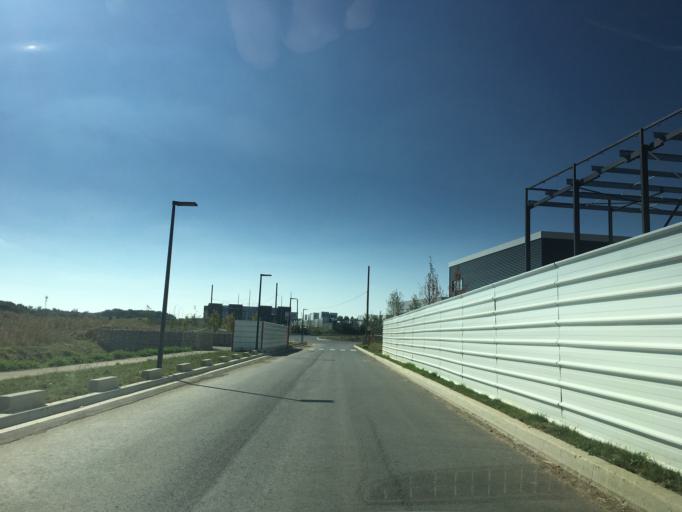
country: FR
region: Ile-de-France
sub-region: Departement de Seine-et-Marne
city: Servon
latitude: 48.7089
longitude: 2.5826
